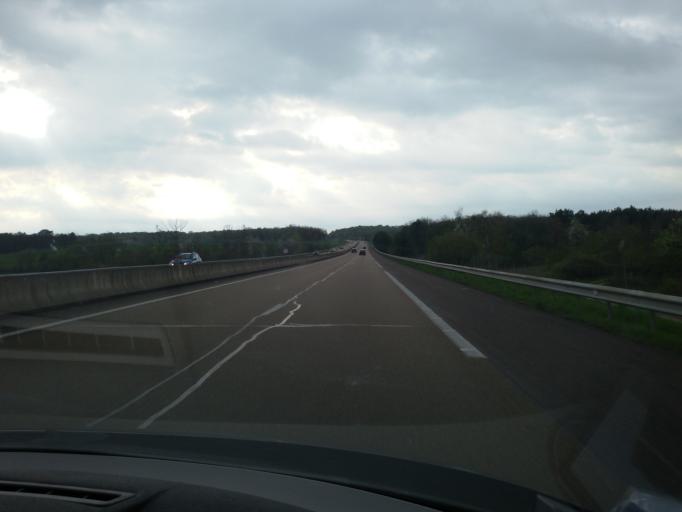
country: FR
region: Champagne-Ardenne
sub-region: Departement de la Haute-Marne
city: Rolampont
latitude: 47.9420
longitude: 5.1920
